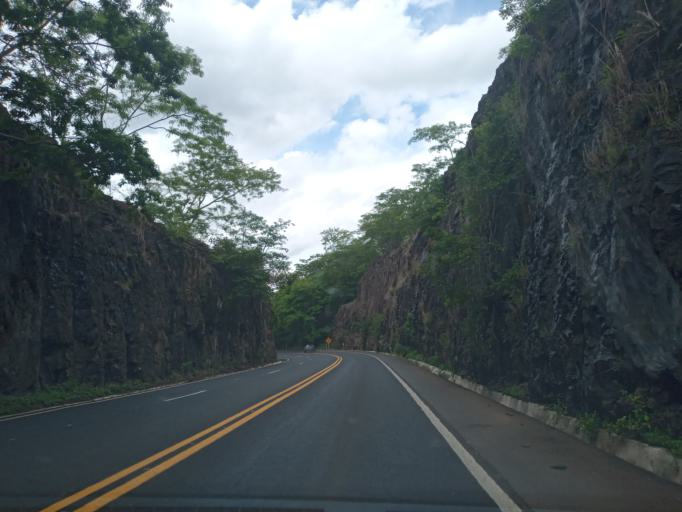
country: BR
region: Minas Gerais
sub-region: Uberaba
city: Uberaba
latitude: -19.2714
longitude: -47.6330
